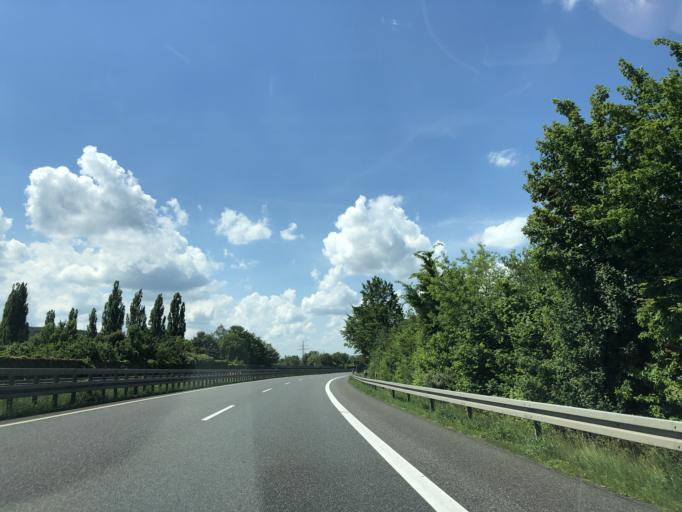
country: DE
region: Hesse
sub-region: Regierungsbezirk Giessen
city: Marburg an der Lahn
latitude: 50.7753
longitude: 8.7592
